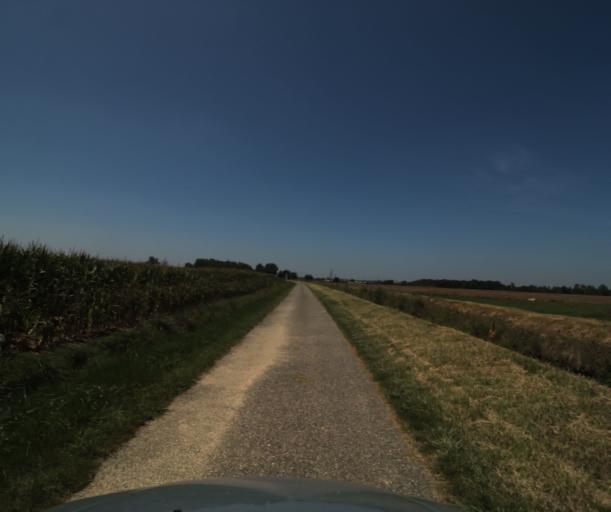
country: FR
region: Midi-Pyrenees
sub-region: Departement de la Haute-Garonne
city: Labastidette
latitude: 43.4618
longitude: 1.2729
